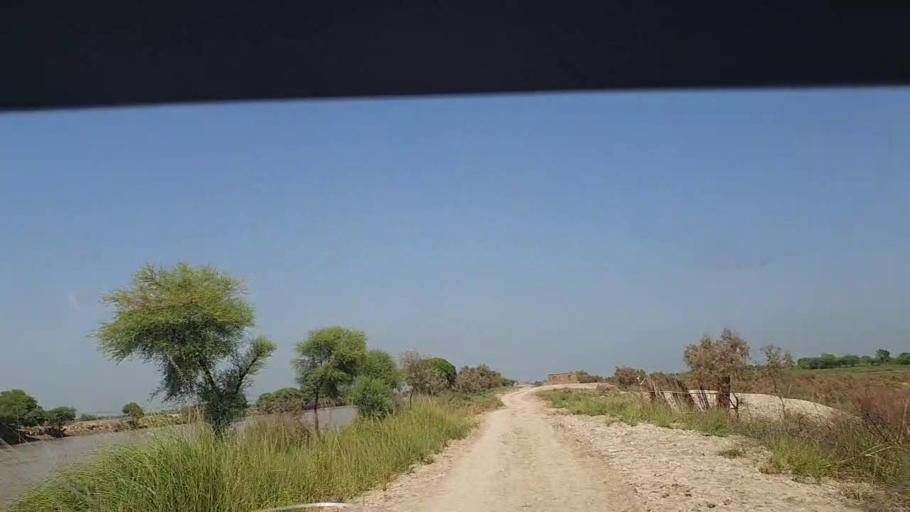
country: PK
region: Sindh
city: Kandhkot
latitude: 28.1836
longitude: 69.1563
